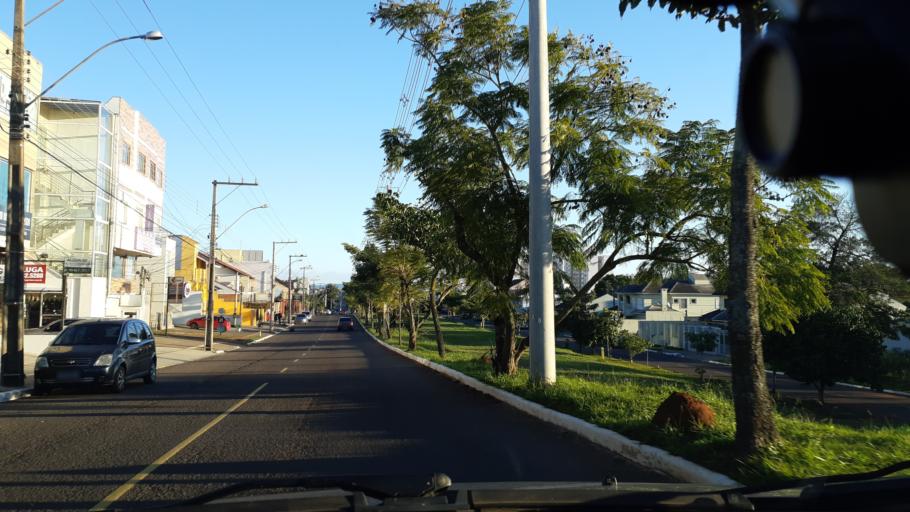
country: BR
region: Rio Grande do Sul
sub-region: Canoas
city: Canoas
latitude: -29.9150
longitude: -51.1543
